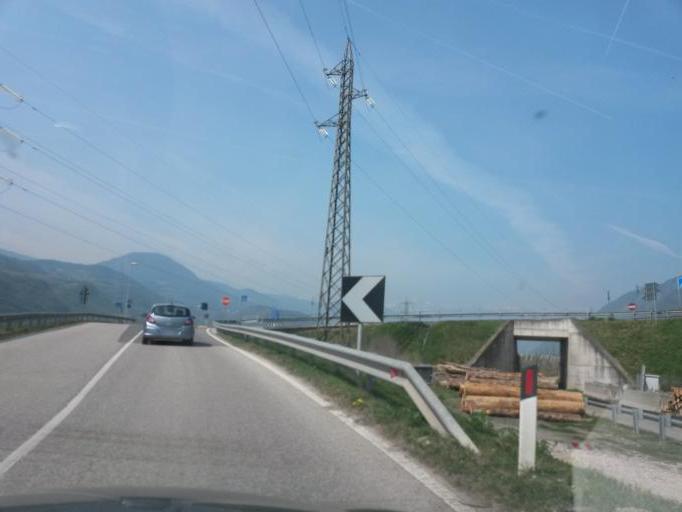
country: IT
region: Trentino-Alto Adige
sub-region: Bolzano
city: Terlano
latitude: 46.5214
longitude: 11.2447
